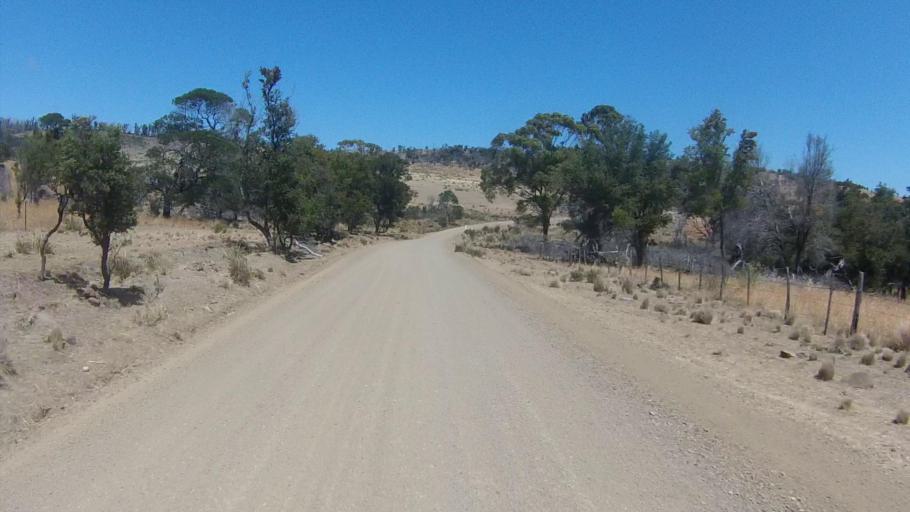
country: AU
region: Tasmania
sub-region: Sorell
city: Sorell
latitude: -42.8948
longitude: 147.8406
